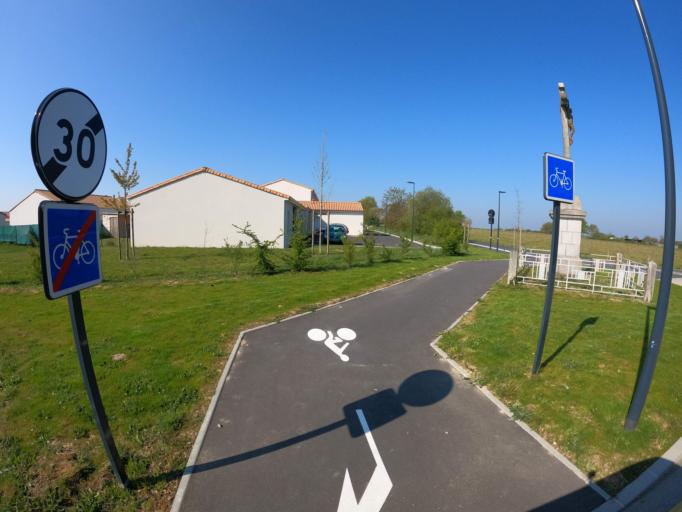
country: FR
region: Pays de la Loire
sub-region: Departement de la Loire-Atlantique
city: Aigrefeuille-sur-Maine
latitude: 47.0872
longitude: -1.4086
